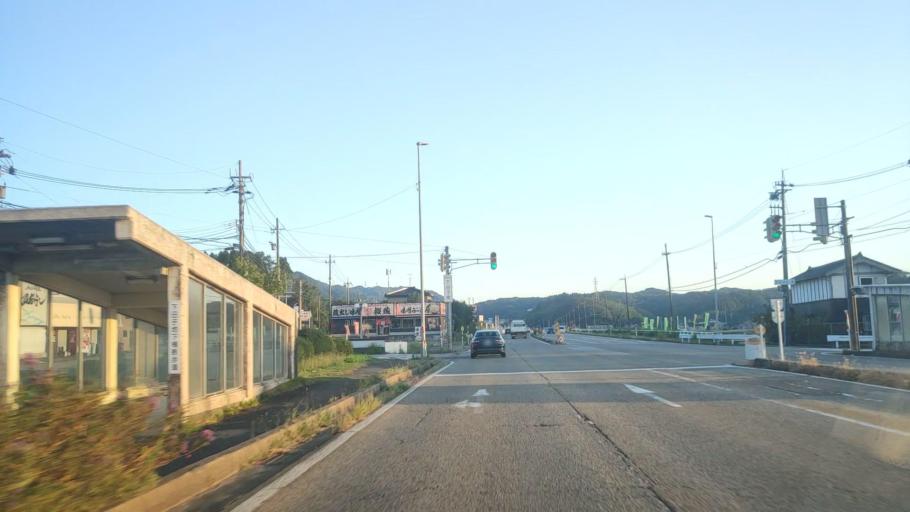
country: JP
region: Toyama
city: Himi
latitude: 36.8166
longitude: 136.9955
